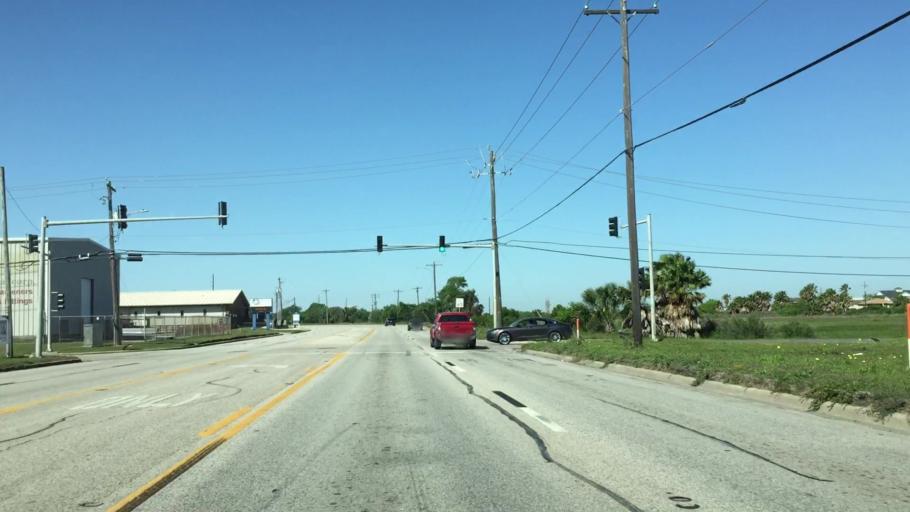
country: US
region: Texas
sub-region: Galveston County
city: Galveston
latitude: 29.2925
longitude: -94.8594
